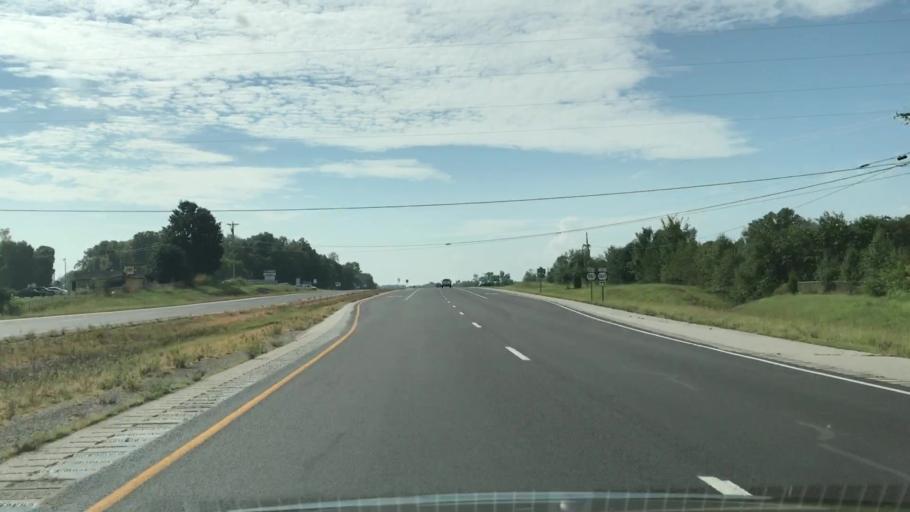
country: US
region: Kentucky
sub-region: Warren County
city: Plano
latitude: 36.8752
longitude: -86.3552
